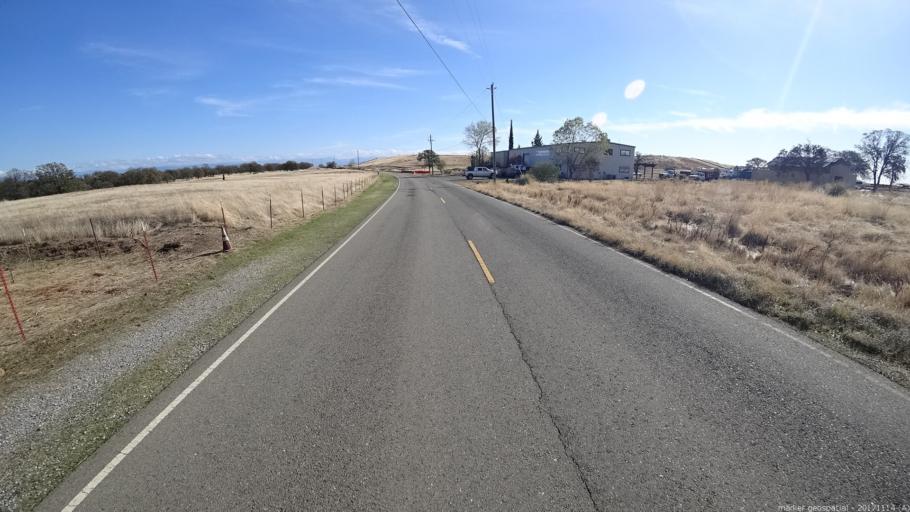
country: US
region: California
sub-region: Shasta County
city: Anderson
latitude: 40.4177
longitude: -122.3636
